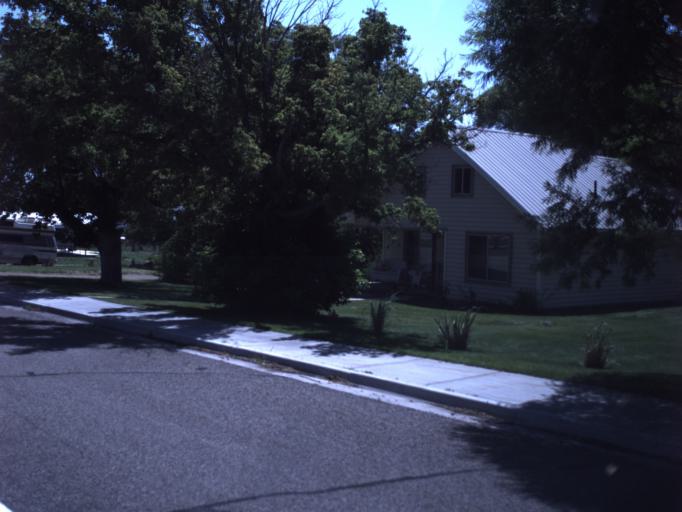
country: US
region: Utah
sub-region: Emery County
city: Ferron
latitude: 38.9231
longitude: -111.2502
